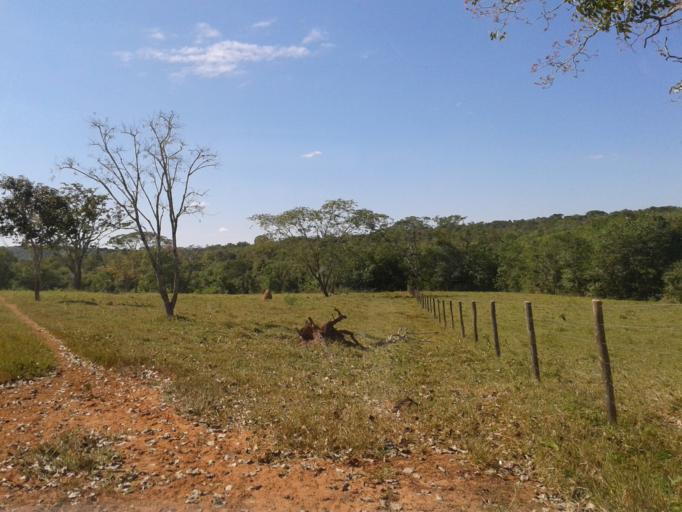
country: BR
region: Minas Gerais
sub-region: Campina Verde
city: Campina Verde
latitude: -19.4012
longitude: -49.7436
